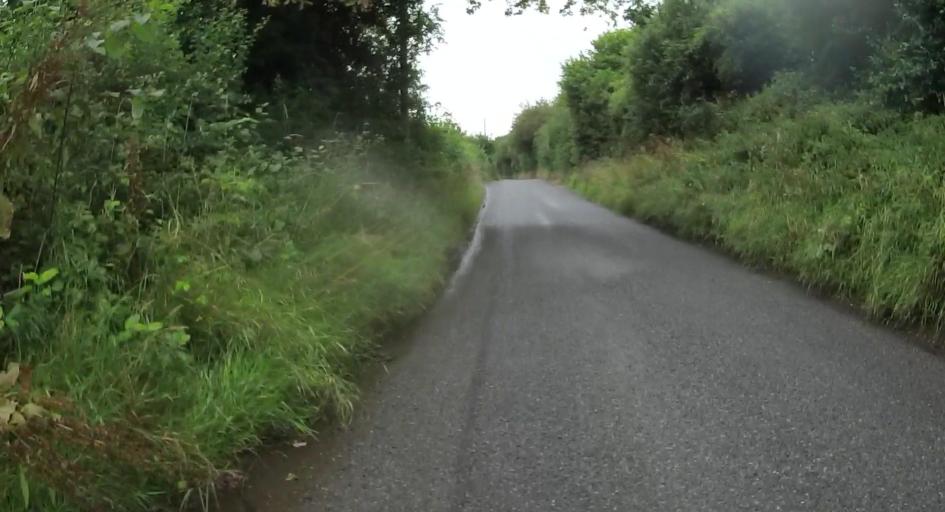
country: GB
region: England
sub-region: Hampshire
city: Highclere
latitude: 51.2533
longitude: -1.3901
